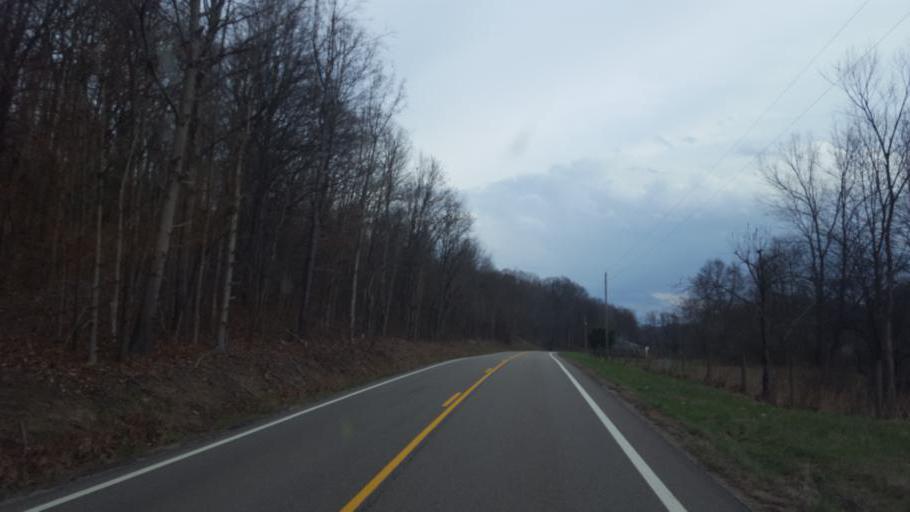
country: US
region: Ohio
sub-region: Guernsey County
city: Mantua
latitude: 40.1343
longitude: -81.7850
